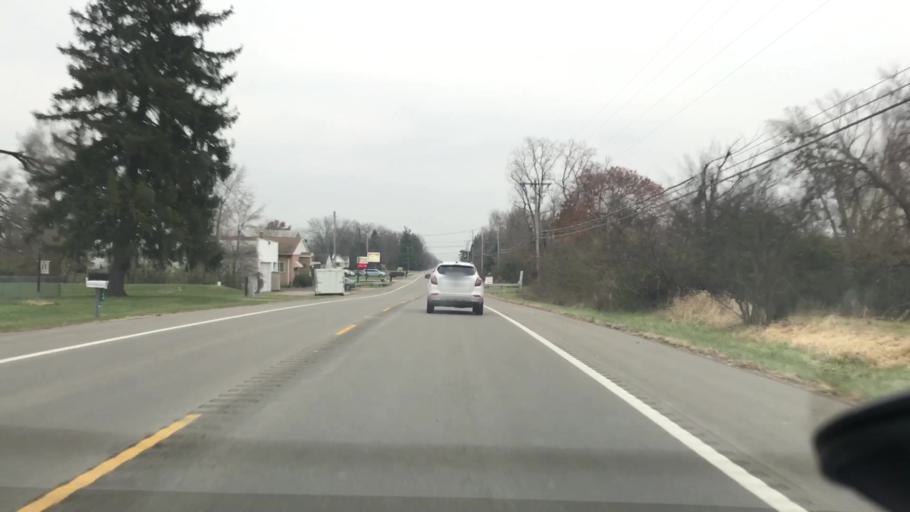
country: US
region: Ohio
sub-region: Greene County
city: Yellow Springs
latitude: 39.8377
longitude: -83.8650
